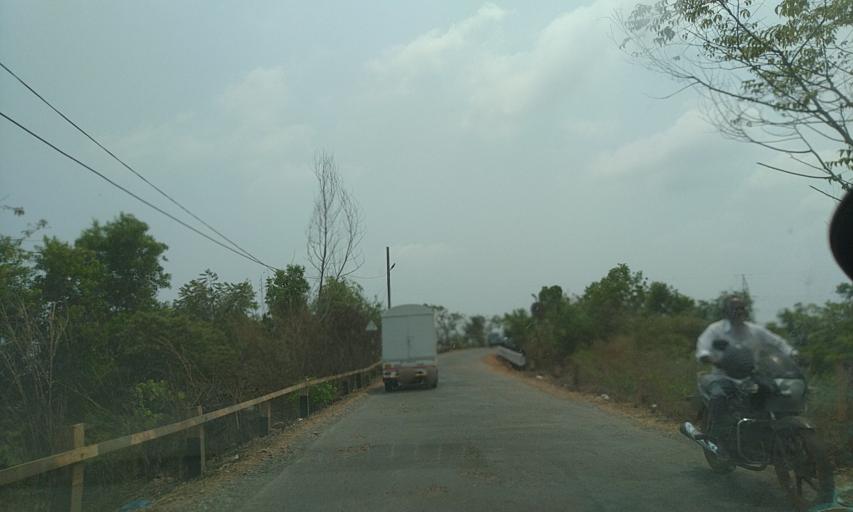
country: IN
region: Goa
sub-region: North Goa
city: Jua
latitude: 15.4855
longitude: 73.9259
